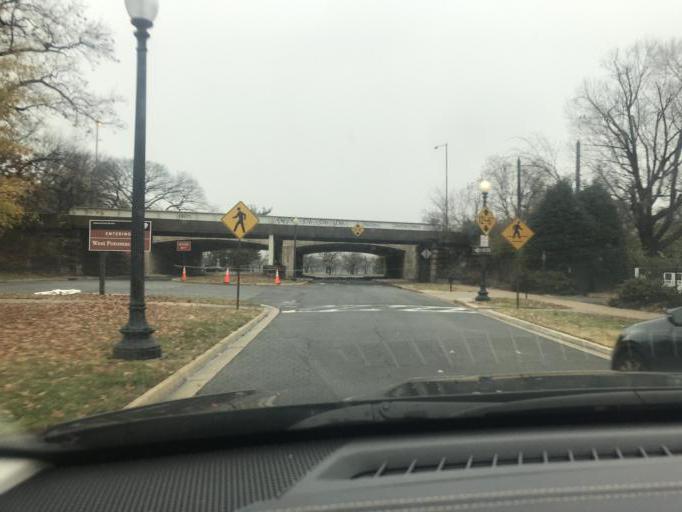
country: US
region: Washington, D.C.
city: Washington, D.C.
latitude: 38.8811
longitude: -77.0327
